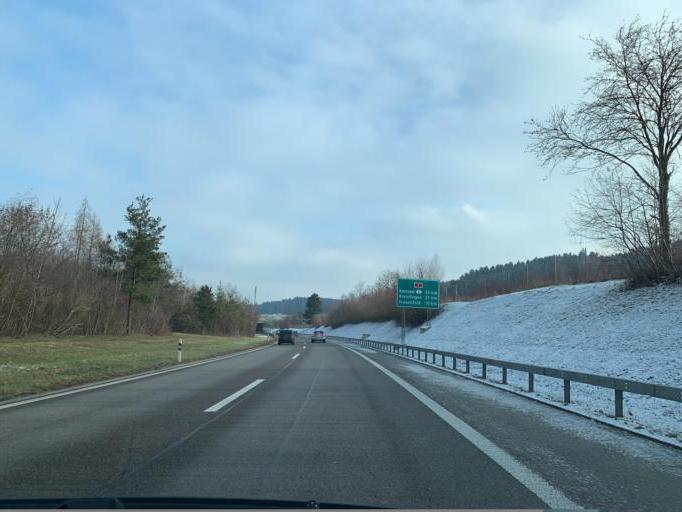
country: CH
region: Zurich
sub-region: Bezirk Winterthur
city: Sulz
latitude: 47.5317
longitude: 8.7938
